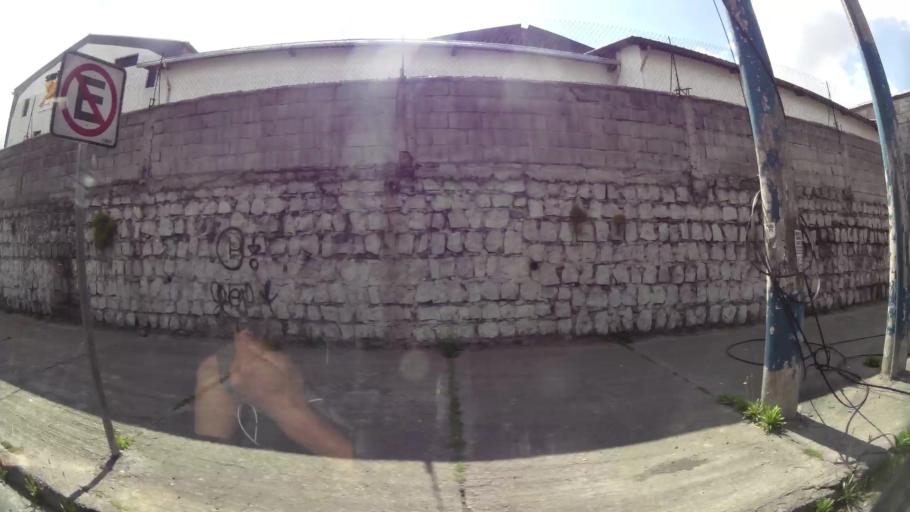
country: EC
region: Pichincha
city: Quito
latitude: -0.1082
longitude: -78.4739
